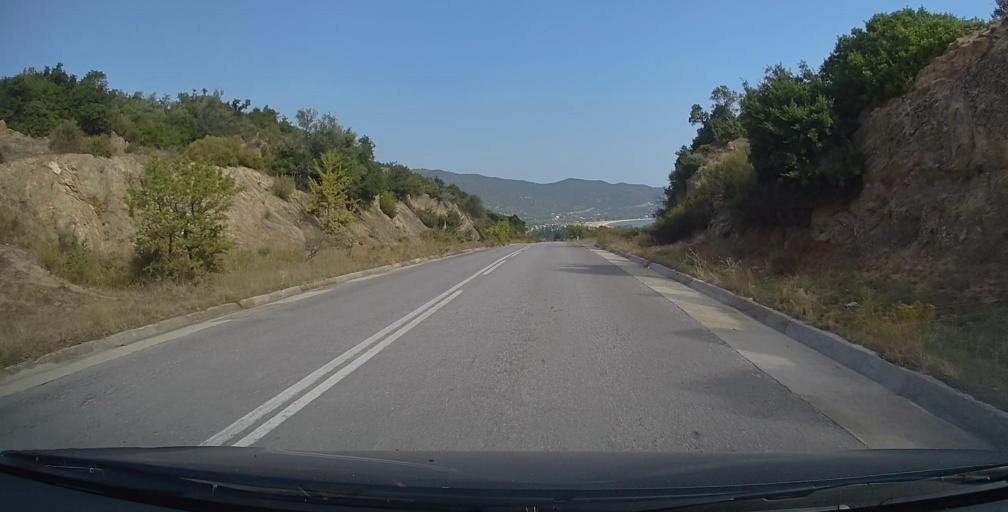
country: GR
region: Central Macedonia
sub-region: Nomos Chalkidikis
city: Sykia
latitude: 40.0253
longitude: 23.9884
